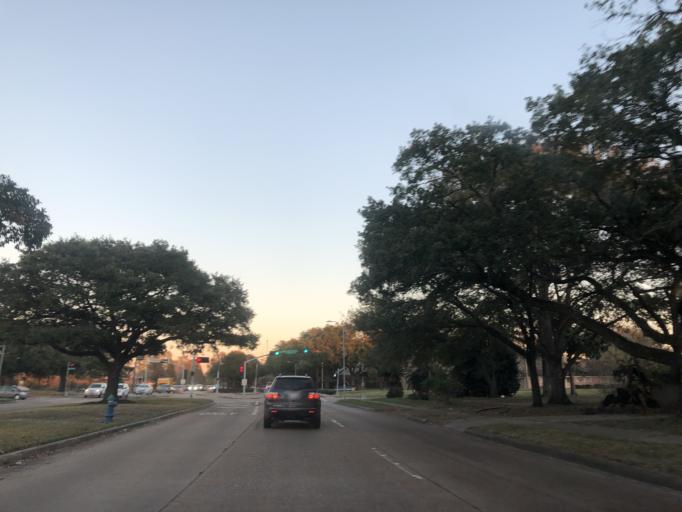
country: US
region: Texas
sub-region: Harris County
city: Bellaire
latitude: 29.6780
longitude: -95.4684
